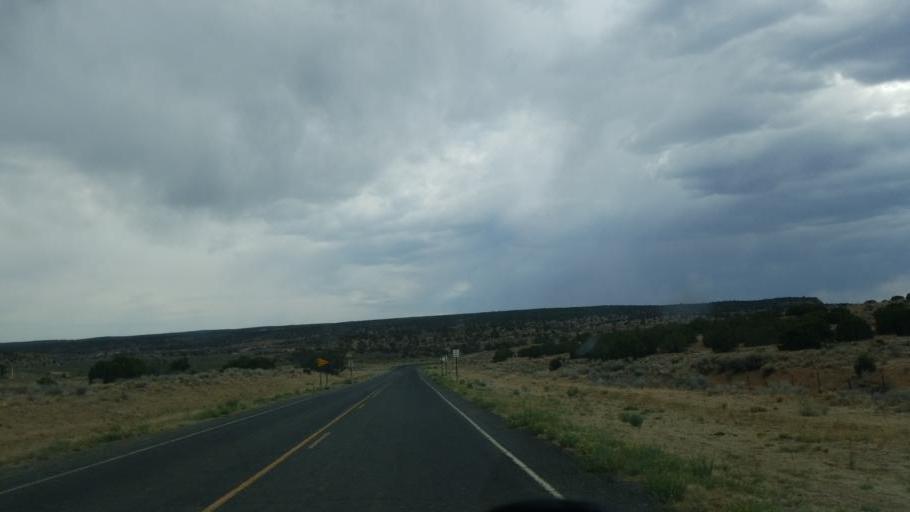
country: US
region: Arizona
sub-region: Apache County
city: Saint Michaels
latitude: 35.4193
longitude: -108.9806
